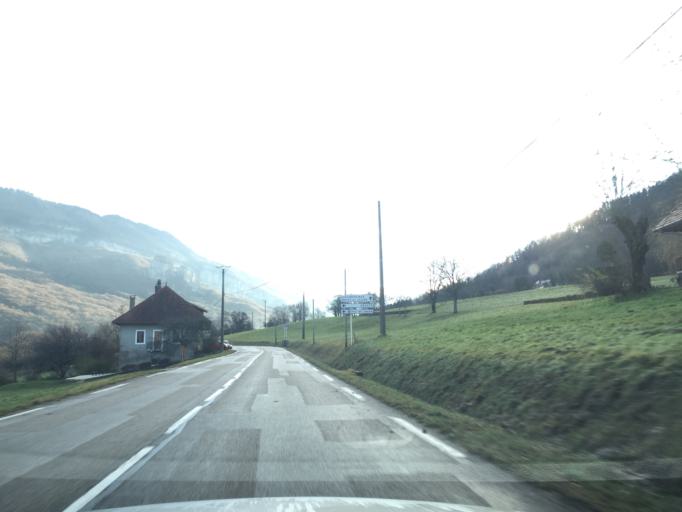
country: FR
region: Rhone-Alpes
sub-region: Departement de la Haute-Savoie
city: Cusy
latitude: 45.7644
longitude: 6.0435
